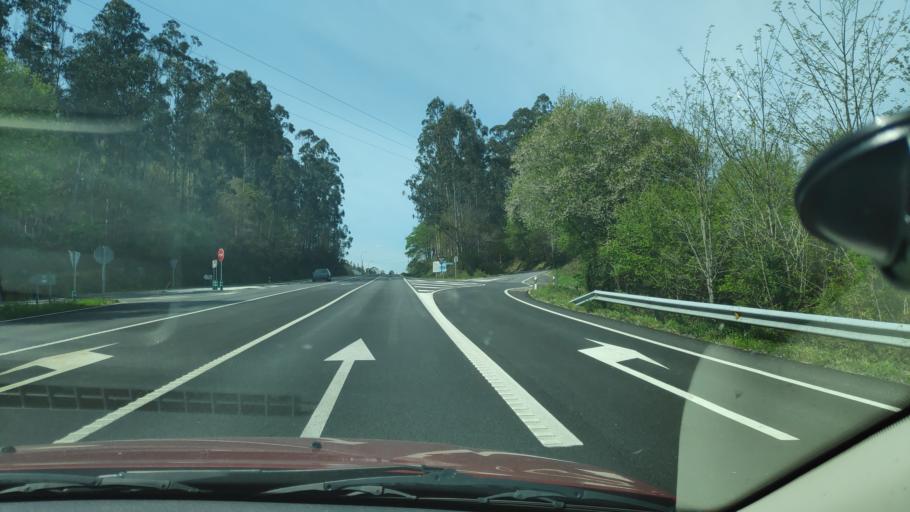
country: ES
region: Galicia
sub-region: Provincia da Coruna
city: Ames
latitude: 42.8781
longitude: -8.6756
